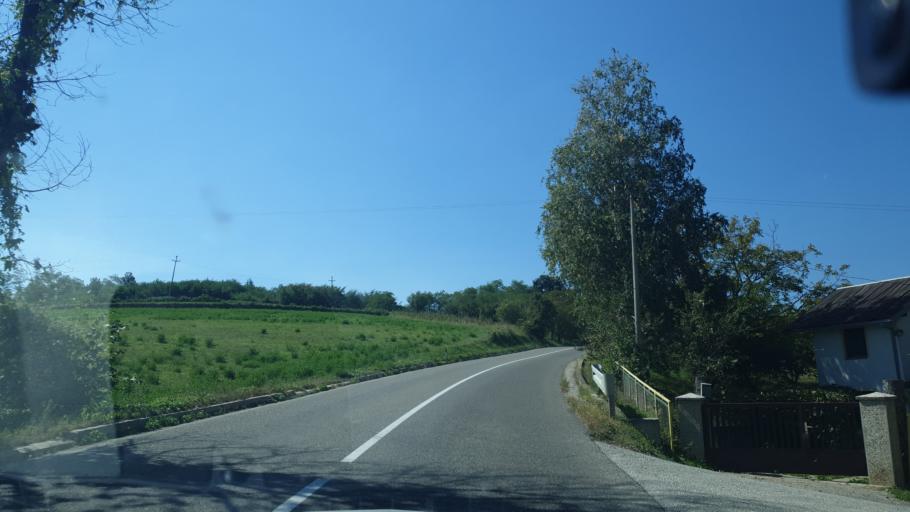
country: RS
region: Central Serbia
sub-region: Kolubarski Okrug
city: Mionica
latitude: 44.1753
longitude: 20.0243
